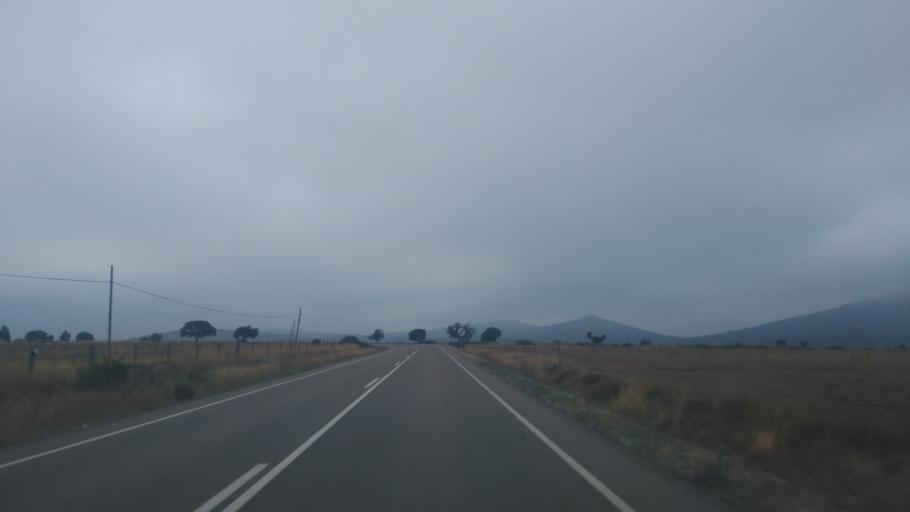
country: ES
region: Castille and Leon
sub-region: Provincia de Salamanca
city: Aldeanueva de la Sierra
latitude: 40.6281
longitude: -6.1075
